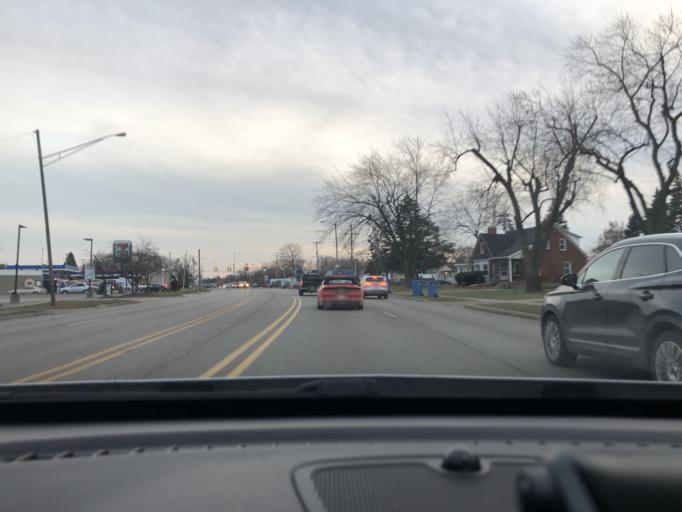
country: US
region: Michigan
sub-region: Wayne County
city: Allen Park
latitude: 42.2712
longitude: -83.2318
